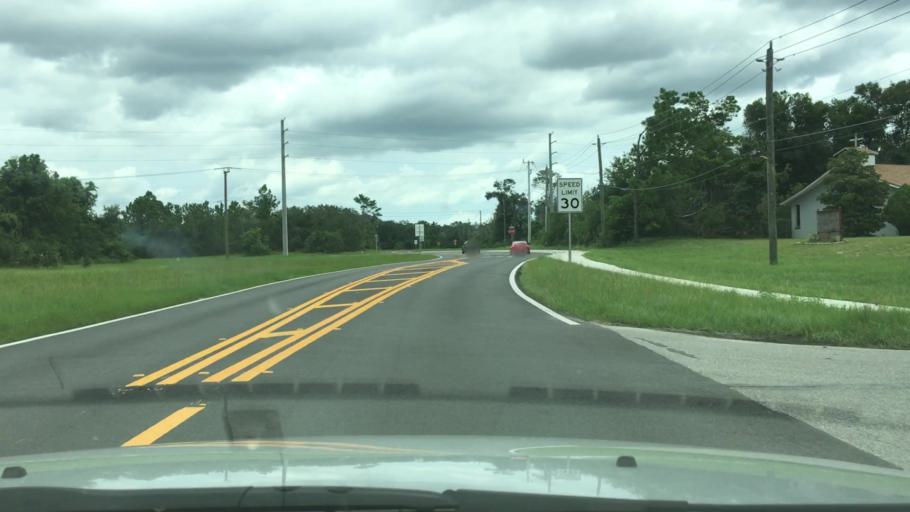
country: US
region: Florida
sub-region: Volusia County
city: Holly Hill
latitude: 29.2325
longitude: -81.0701
